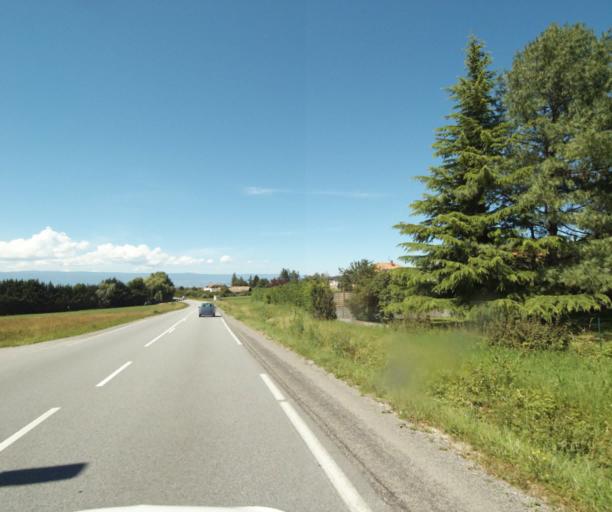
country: FR
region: Rhone-Alpes
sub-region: Departement de la Haute-Savoie
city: Loisin
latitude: 46.2789
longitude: 6.3112
